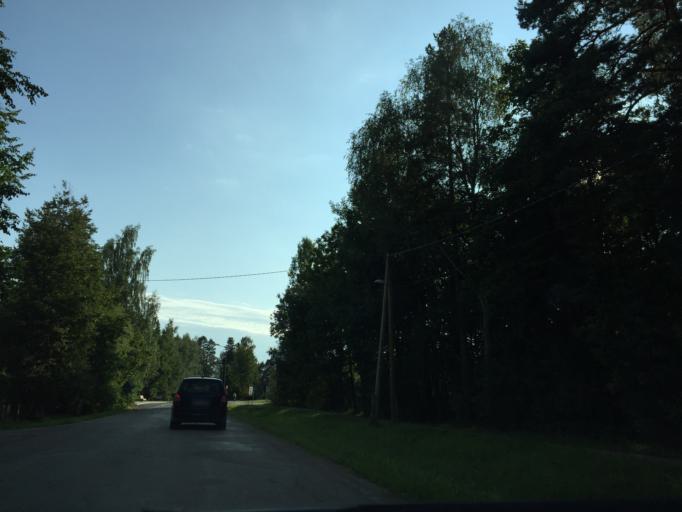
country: LV
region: Ogre
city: Ogre
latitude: 56.8211
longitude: 24.6592
